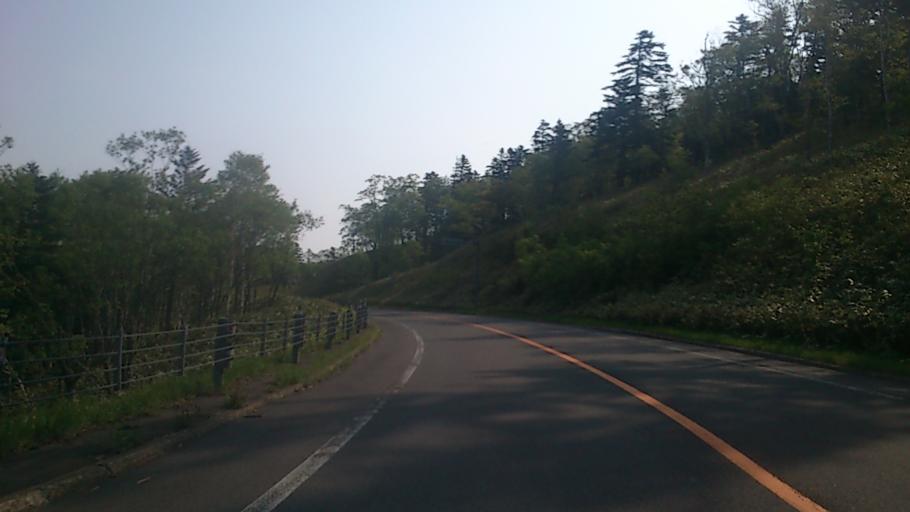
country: JP
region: Hokkaido
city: Bihoro
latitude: 43.4473
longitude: 144.1979
